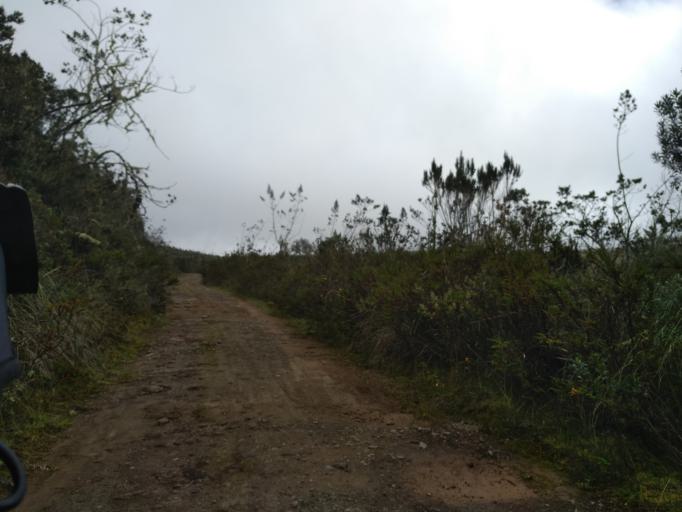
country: EC
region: Carchi
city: San Gabriel
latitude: 0.6947
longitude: -77.8489
